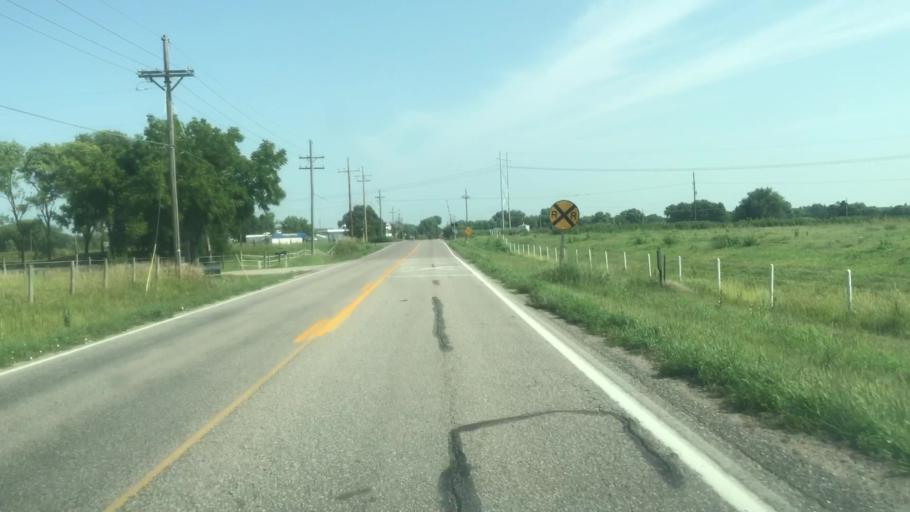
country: US
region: Nebraska
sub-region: Hall County
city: Grand Island
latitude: 40.9124
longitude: -98.3018
